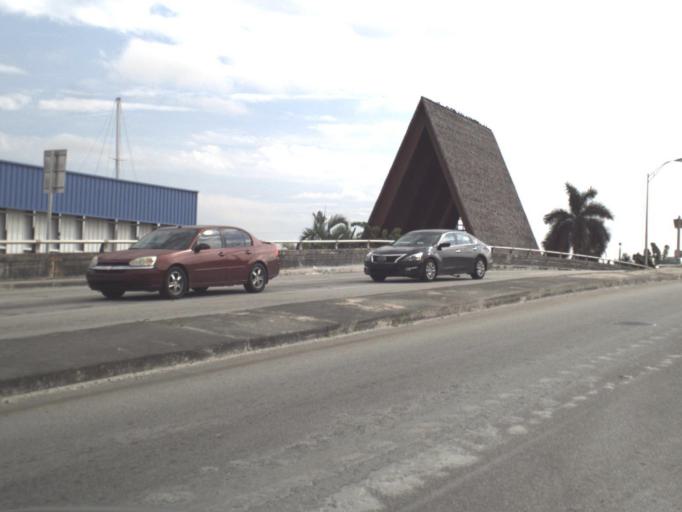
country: US
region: Florida
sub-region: Miami-Dade County
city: Brownsville
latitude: 25.7949
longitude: -80.2562
